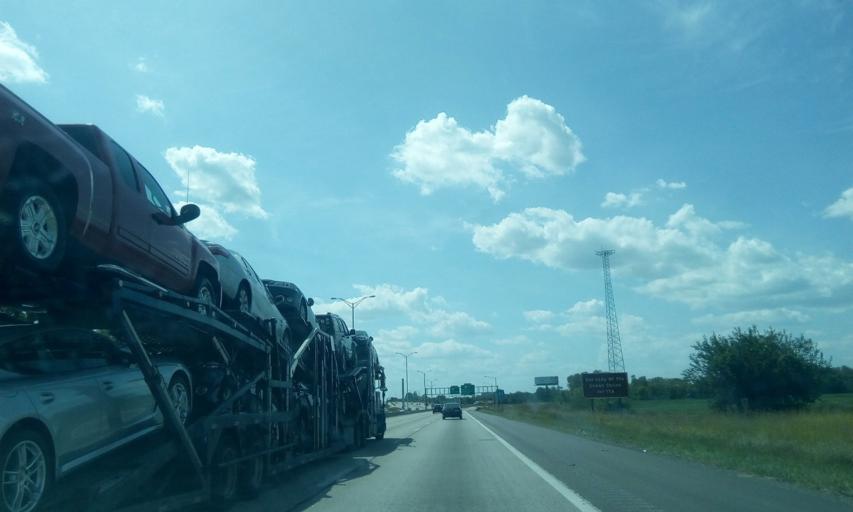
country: US
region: Illinois
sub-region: Saint Clair County
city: Alorton
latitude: 38.5873
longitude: -90.1000
